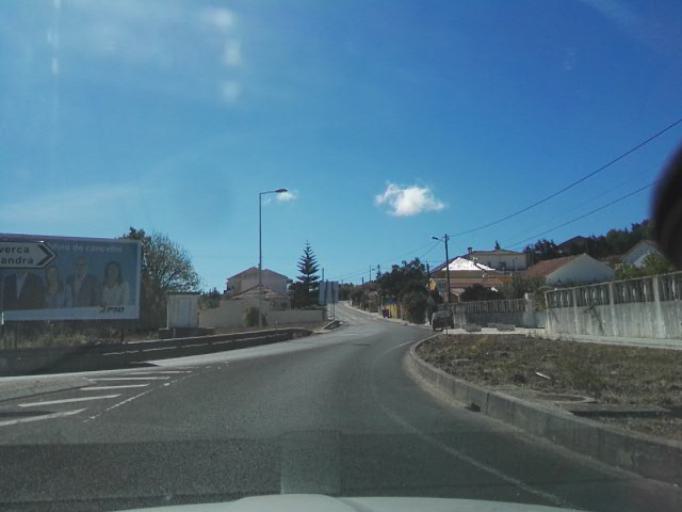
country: PT
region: Lisbon
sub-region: Arruda Dos Vinhos
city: Arruda dos Vinhos
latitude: 38.9631
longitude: -9.0617
